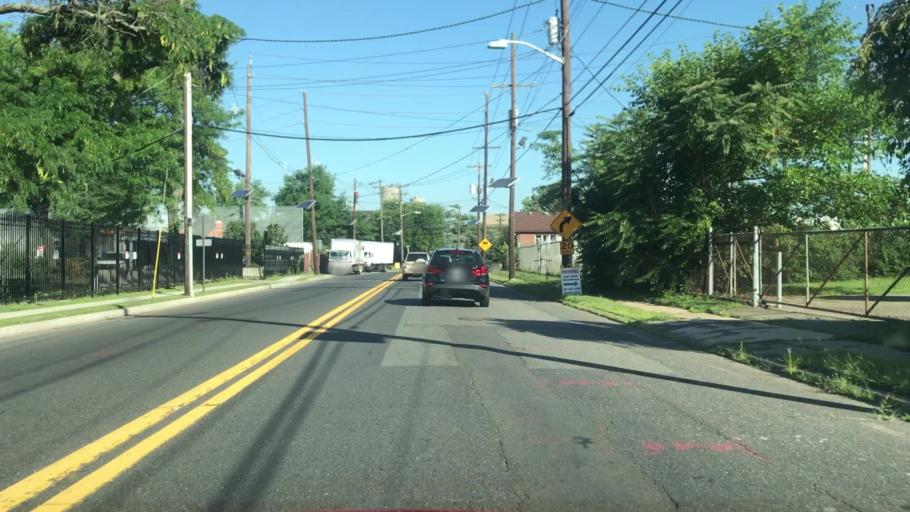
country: US
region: New Jersey
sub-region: Bergen County
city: Ridgefield
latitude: 40.8353
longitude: -74.0167
